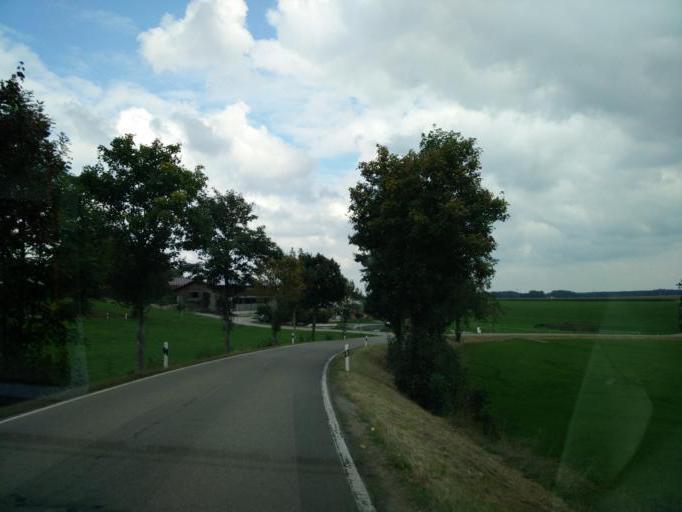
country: DE
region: Baden-Wuerttemberg
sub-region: Tuebingen Region
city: Bad Wurzach
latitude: 47.9472
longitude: 9.9146
